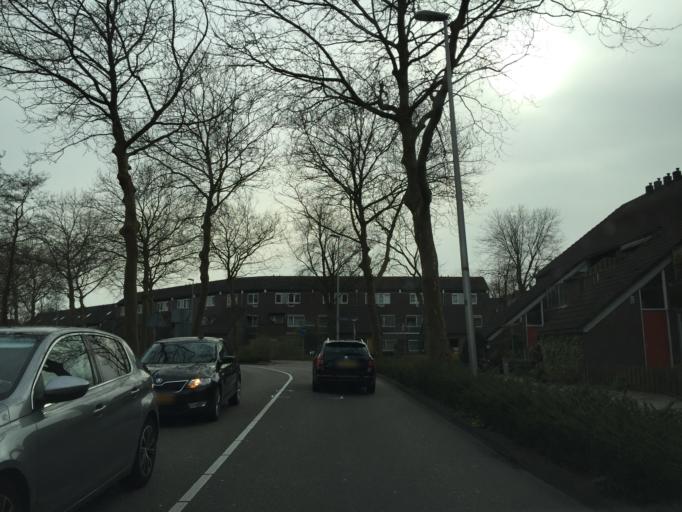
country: NL
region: South Holland
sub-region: Gemeente Zoetermeer
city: Zoetermeer
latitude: 52.0626
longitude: 4.5160
